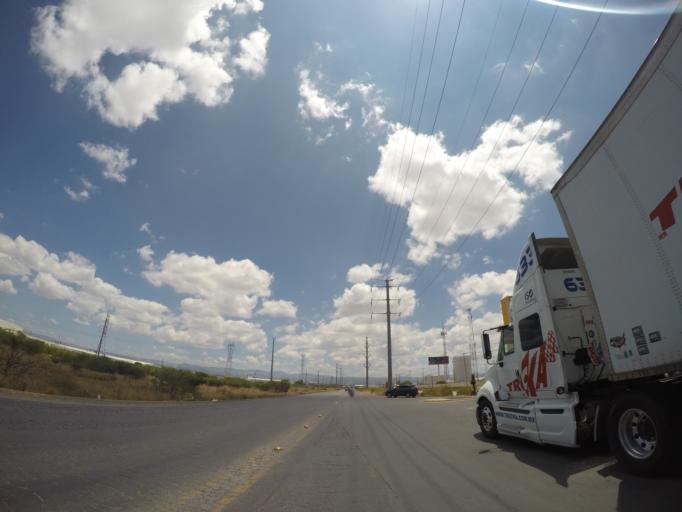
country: MX
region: San Luis Potosi
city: La Pila
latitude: 22.0420
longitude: -100.8927
